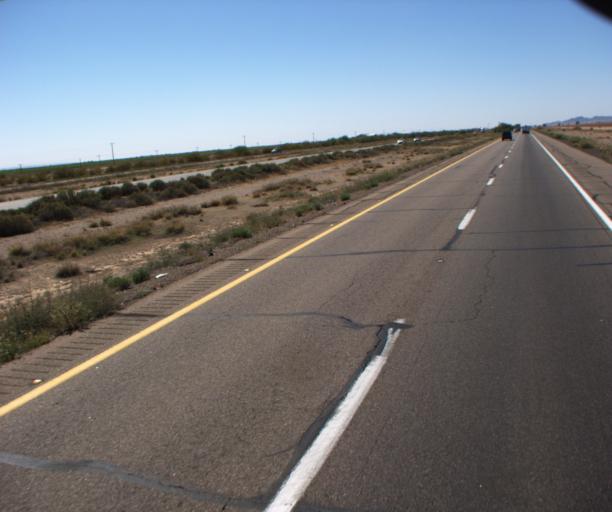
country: US
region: Arizona
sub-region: Maricopa County
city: Gila Bend
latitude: 32.9276
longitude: -112.8453
